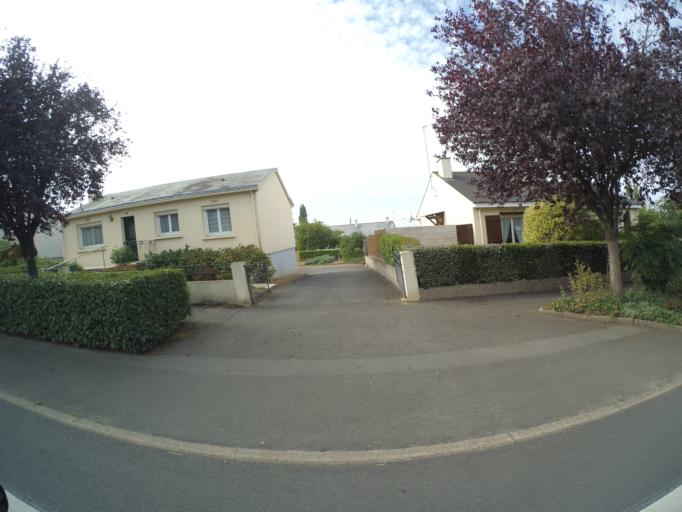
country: FR
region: Pays de la Loire
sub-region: Departement de Maine-et-Loire
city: Chemille-Melay
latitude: 47.2147
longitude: -0.7225
